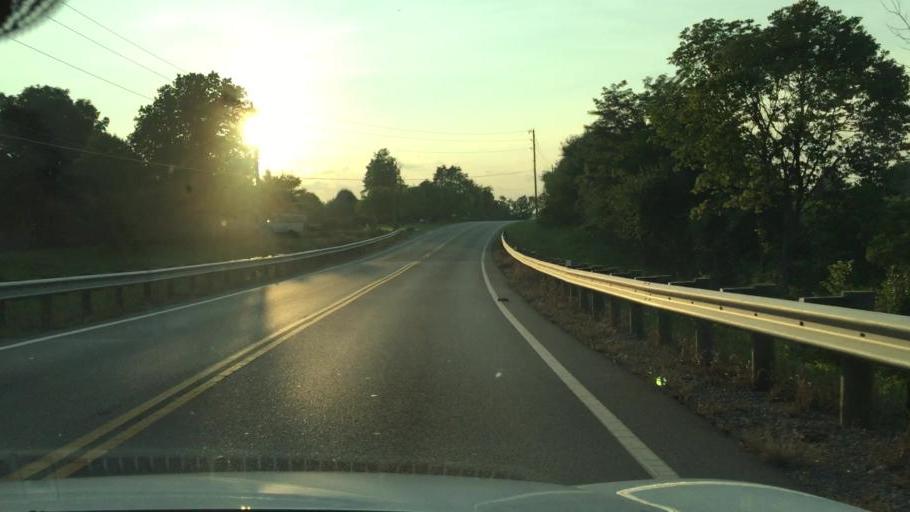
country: US
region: Ohio
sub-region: Madison County
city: West Jefferson
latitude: 39.9623
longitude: -83.3545
